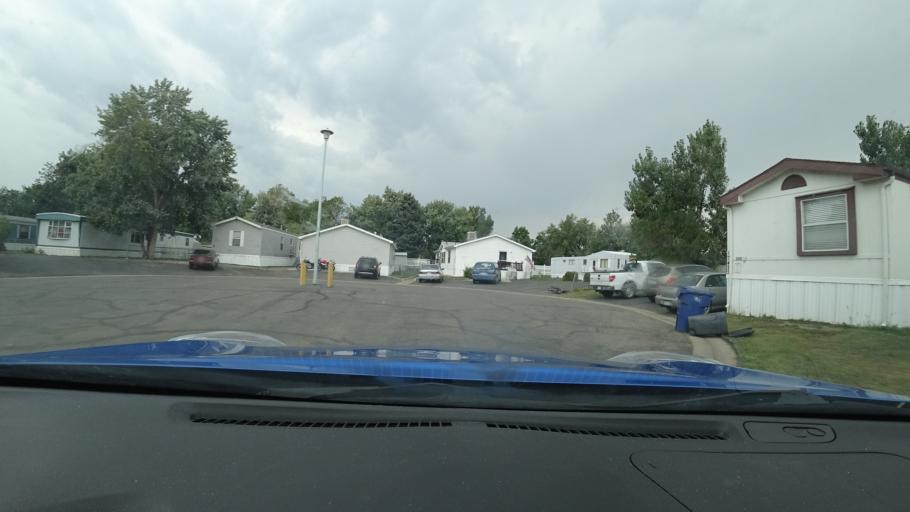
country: US
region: Colorado
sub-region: Adams County
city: Aurora
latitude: 39.7417
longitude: -104.7858
